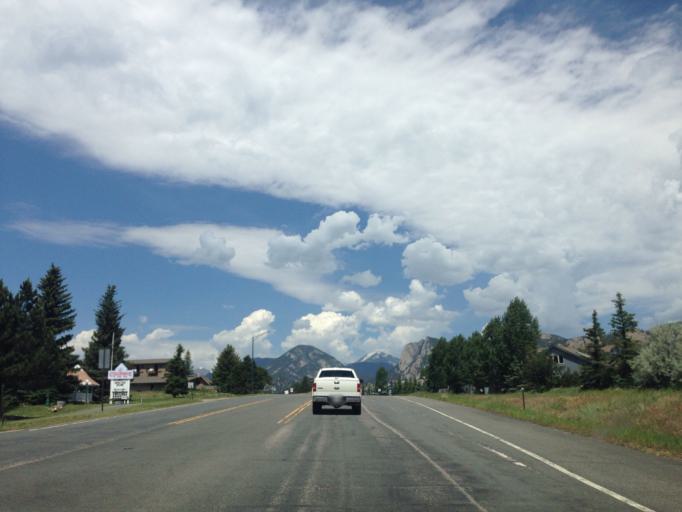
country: US
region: Colorado
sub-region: Larimer County
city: Estes Park
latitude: 40.3817
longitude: -105.4957
